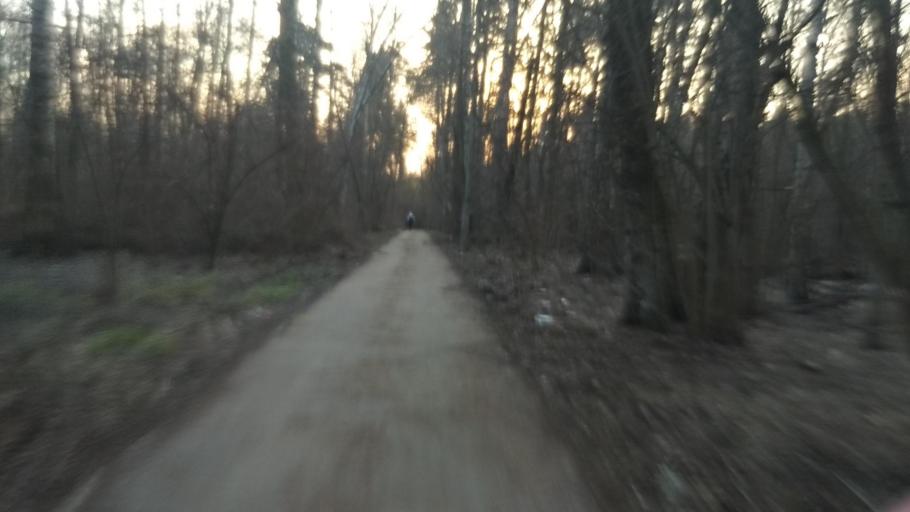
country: RU
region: Moskovskaya
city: Vidnoye
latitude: 55.5599
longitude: 37.7395
